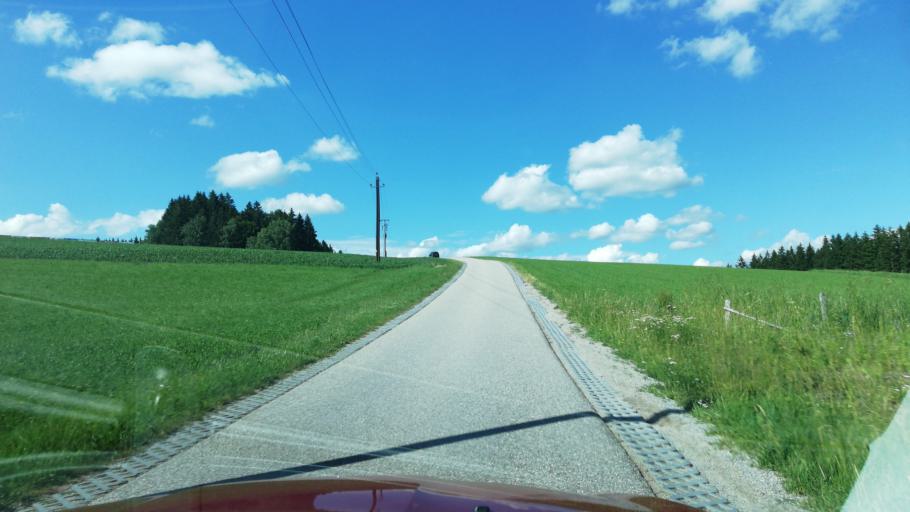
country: AT
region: Upper Austria
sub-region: Politischer Bezirk Urfahr-Umgebung
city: Sonnberg im Muehlkreis
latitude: 48.4601
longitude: 14.3275
